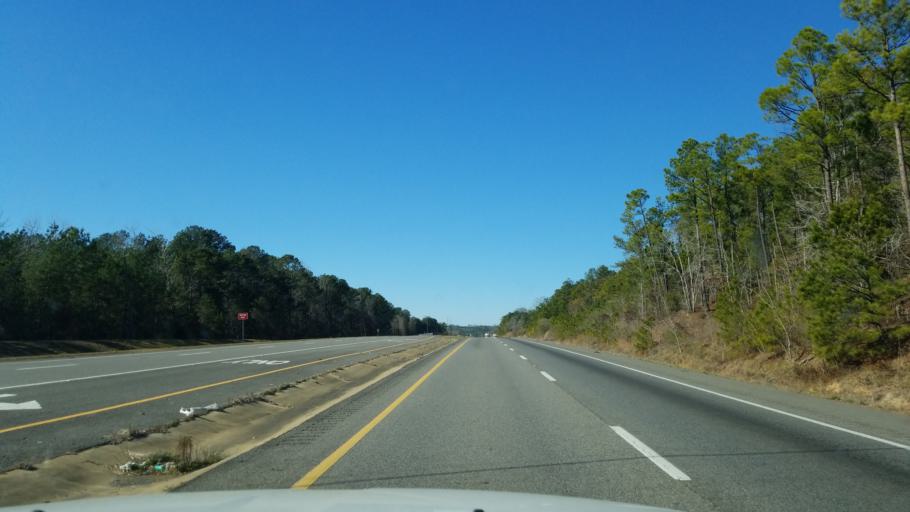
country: US
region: Alabama
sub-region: Tuscaloosa County
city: Northport
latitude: 33.2563
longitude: -87.6948
